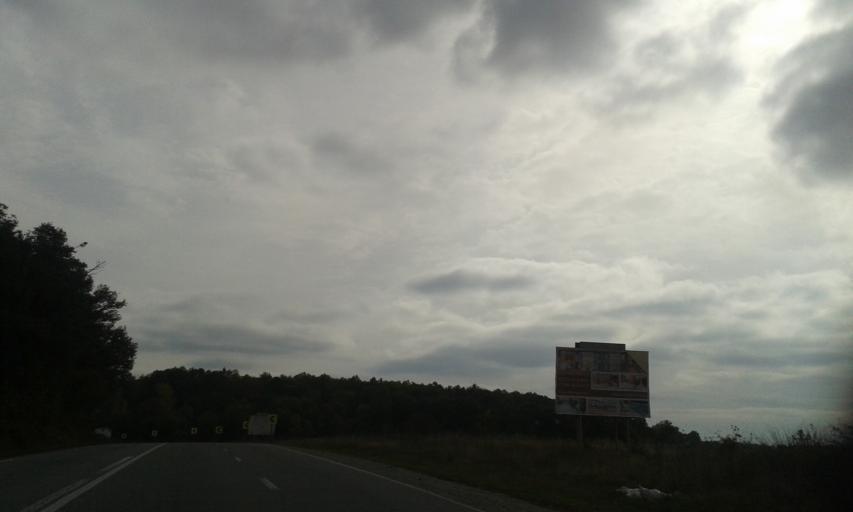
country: RO
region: Gorj
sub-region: Comuna Balanesti
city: Balanesti
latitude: 45.0341
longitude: 23.3753
